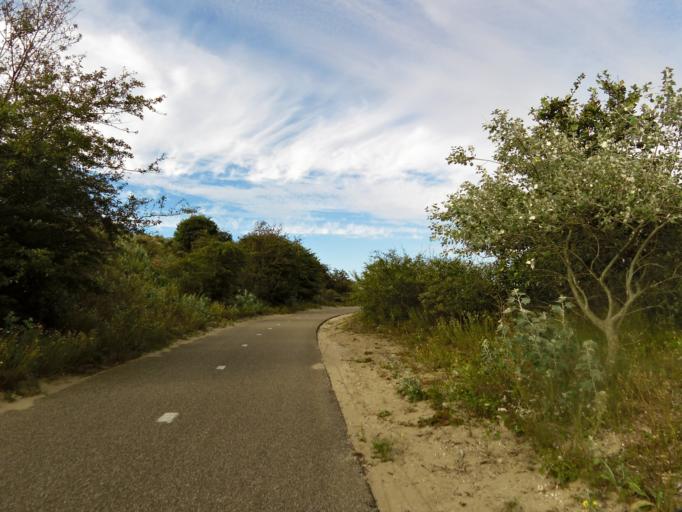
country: NL
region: South Holland
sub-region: Gemeente Wassenaar
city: Wassenaar
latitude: 52.1643
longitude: 4.3616
